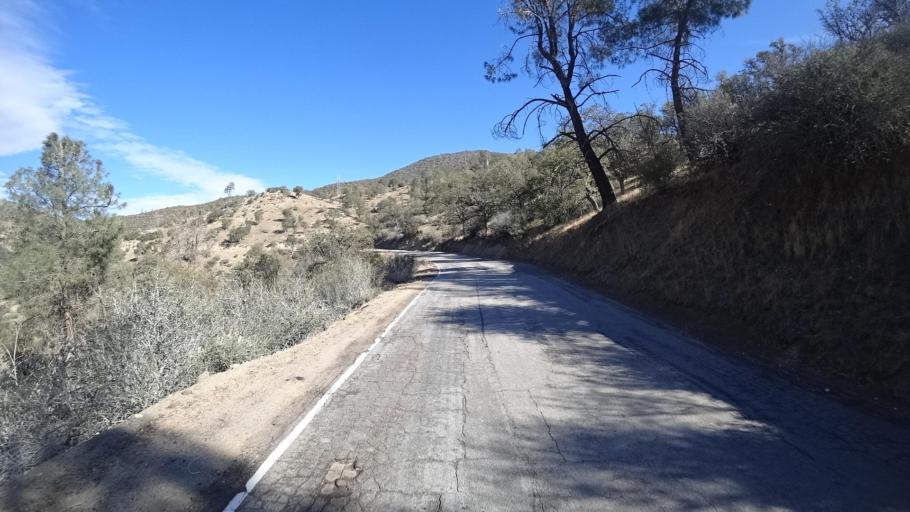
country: US
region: California
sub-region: Kern County
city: Bodfish
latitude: 35.5582
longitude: -118.5091
